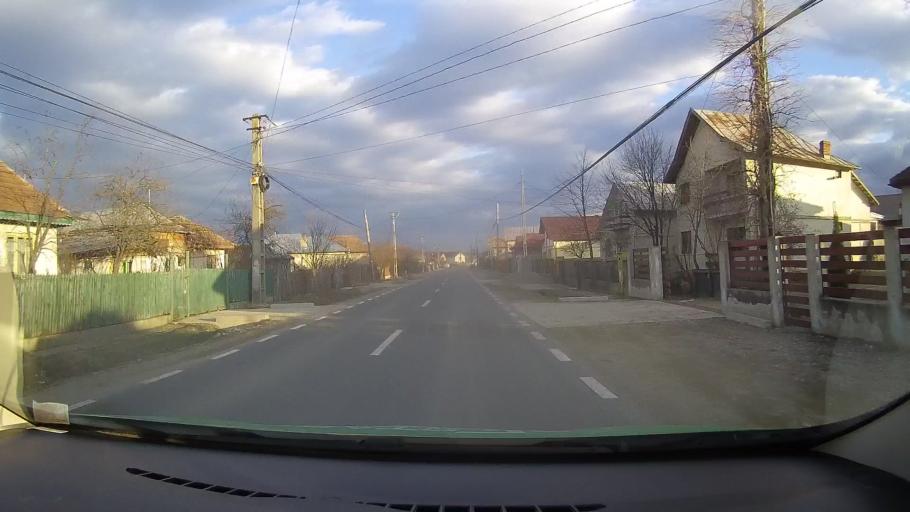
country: RO
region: Dambovita
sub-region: Comuna I. L. Caragiale
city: Ghirdoveni
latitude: 44.9415
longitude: 25.6700
